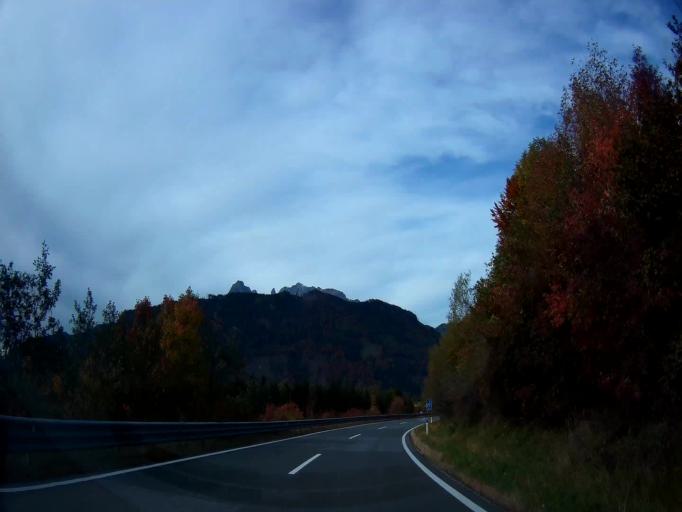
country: AT
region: Salzburg
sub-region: Politischer Bezirk Sankt Johann im Pongau
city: Bischofshofen
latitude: 47.4369
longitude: 13.2321
